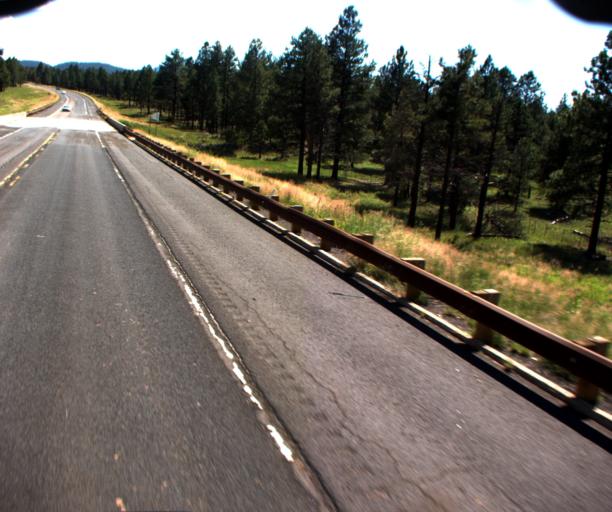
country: US
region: Arizona
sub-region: Coconino County
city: Williams
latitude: 35.2871
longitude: -112.1441
